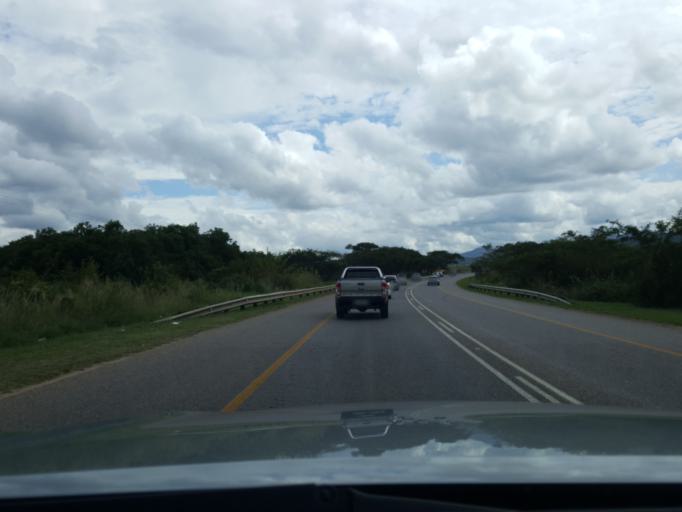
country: ZA
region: Mpumalanga
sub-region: Ehlanzeni District
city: Nelspruit
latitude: -25.4523
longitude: 30.9278
